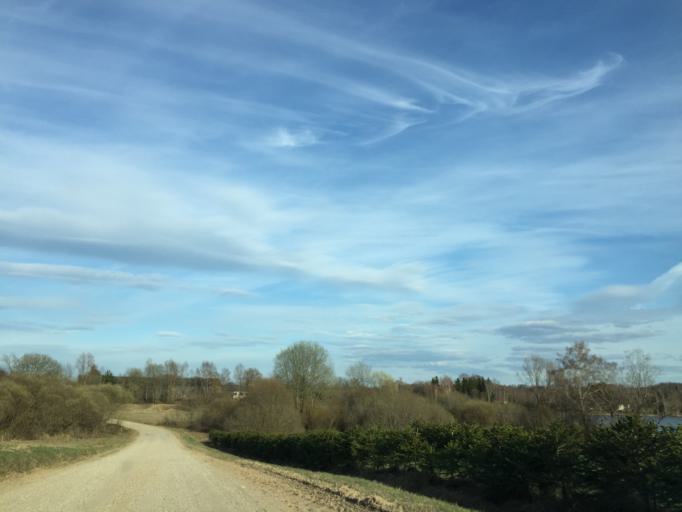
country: EE
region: Tartu
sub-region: Noo vald
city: Noo
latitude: 58.1829
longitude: 26.5614
